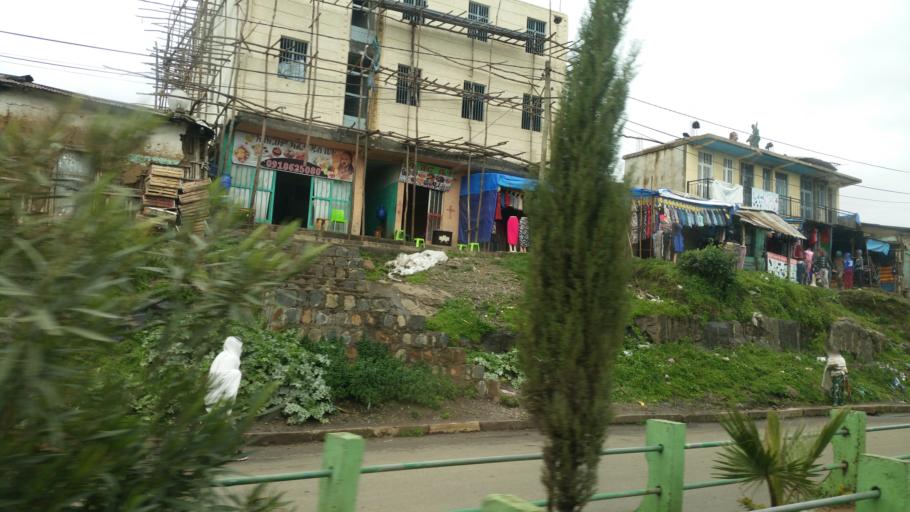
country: ET
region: Amhara
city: Debark'
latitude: 13.1559
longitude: 37.8984
